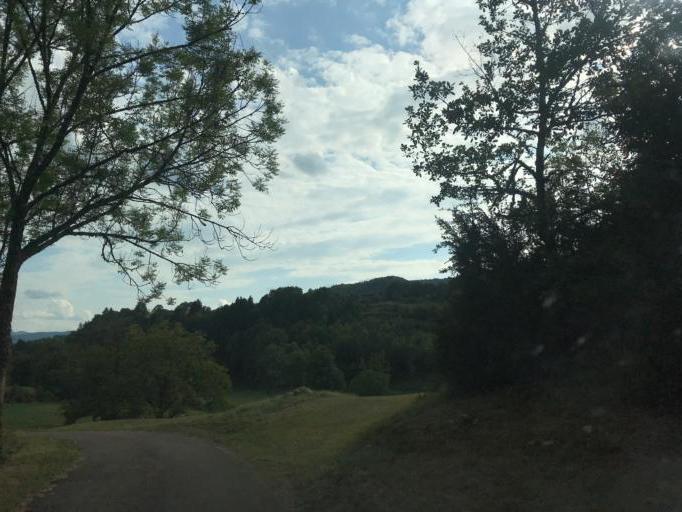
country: FR
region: Franche-Comte
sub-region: Departement du Jura
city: Saint-Lupicin
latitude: 46.4312
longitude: 5.8086
